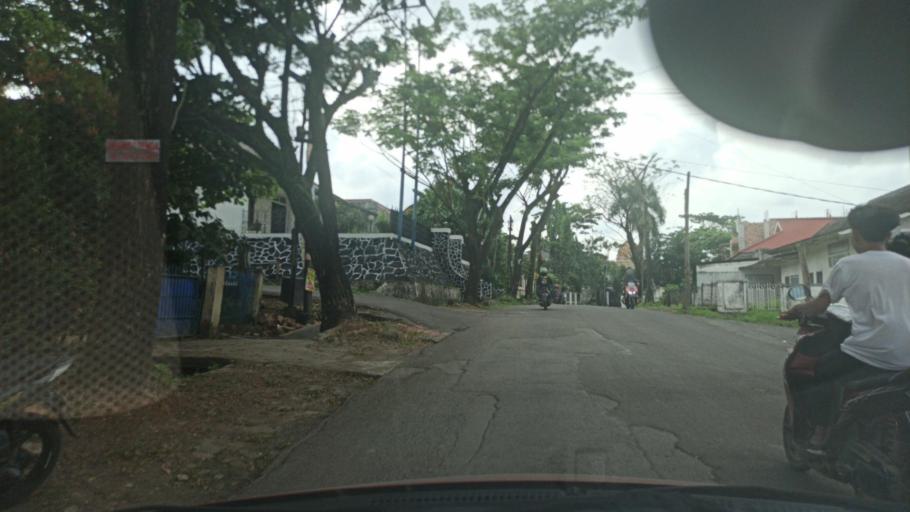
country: ID
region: South Sumatra
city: Plaju
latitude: -2.9899
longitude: 104.7421
